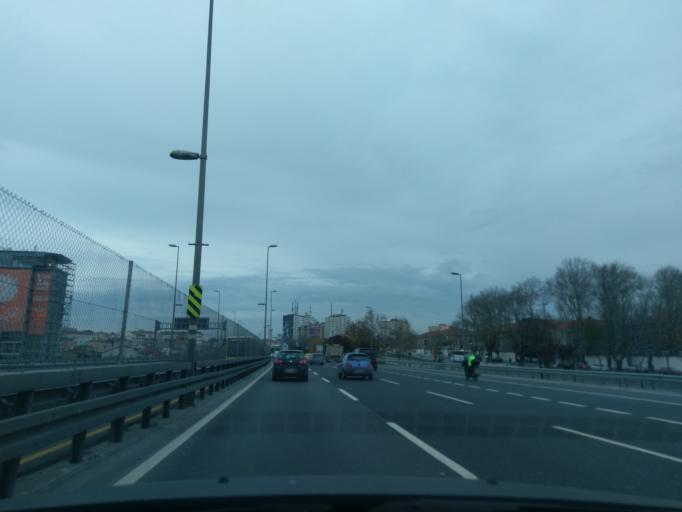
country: TR
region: Istanbul
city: Sisli
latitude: 41.0592
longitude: 28.9649
